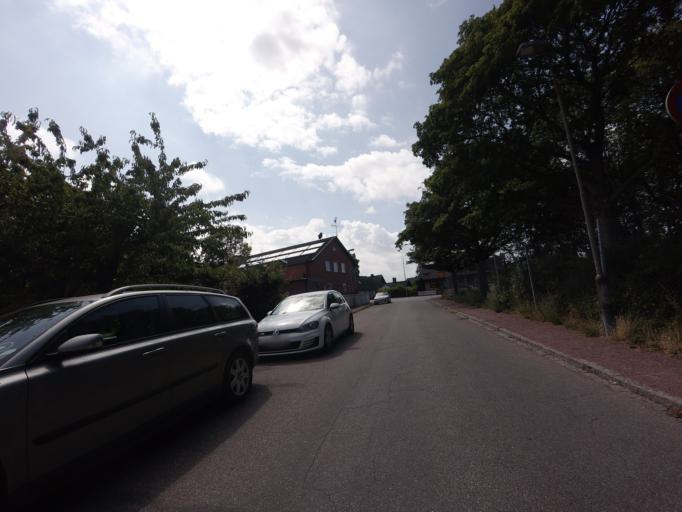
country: SE
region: Skane
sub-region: Malmo
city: Malmoe
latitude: 55.5695
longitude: 12.9974
